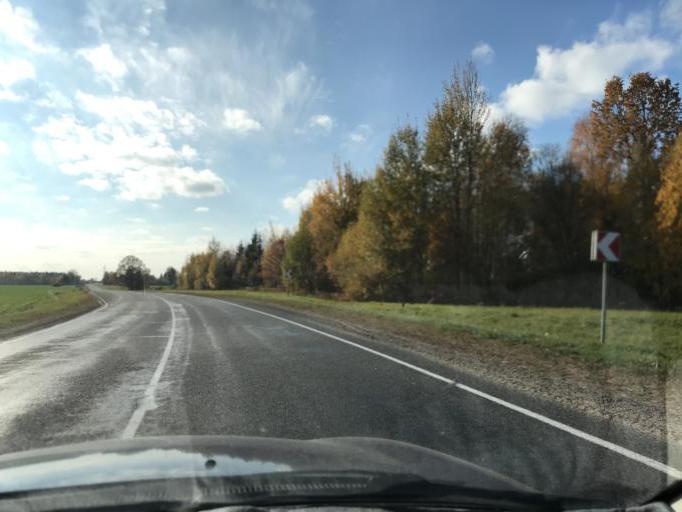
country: BY
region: Grodnenskaya
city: Voranava
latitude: 54.1838
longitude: 25.3365
